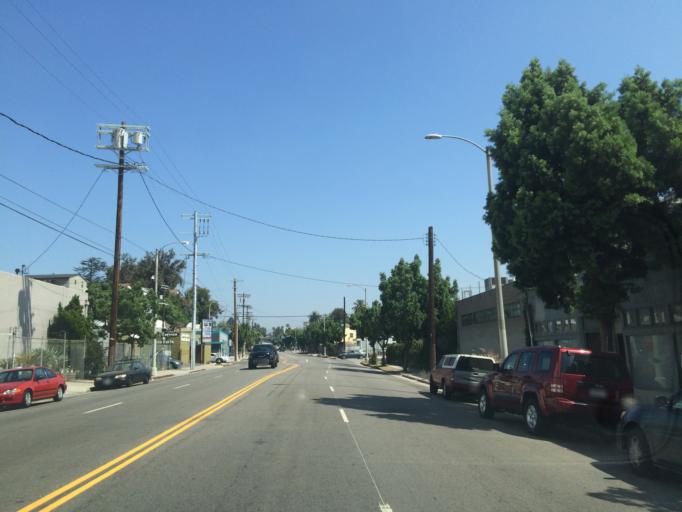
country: US
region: California
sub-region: Los Angeles County
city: Echo Park
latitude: 34.0635
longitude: -118.2598
